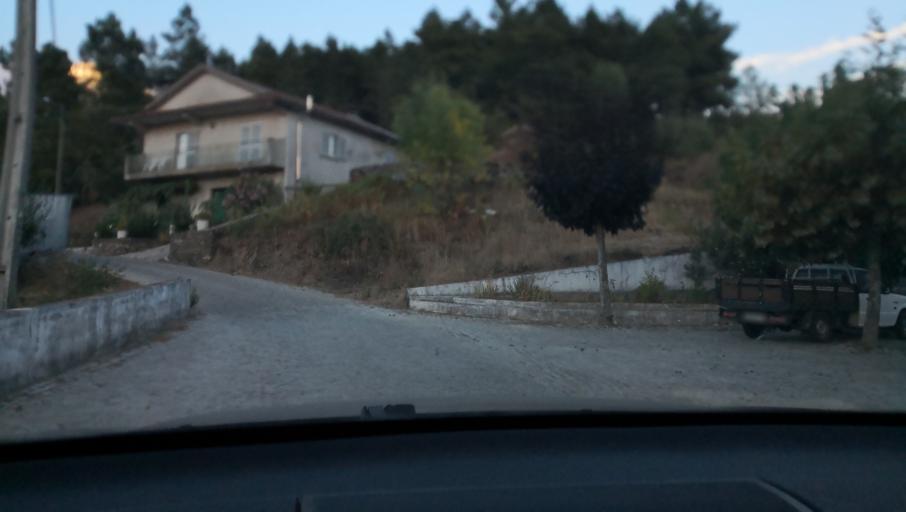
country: PT
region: Vila Real
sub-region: Sabrosa
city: Vilela
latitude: 41.2363
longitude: -7.6146
